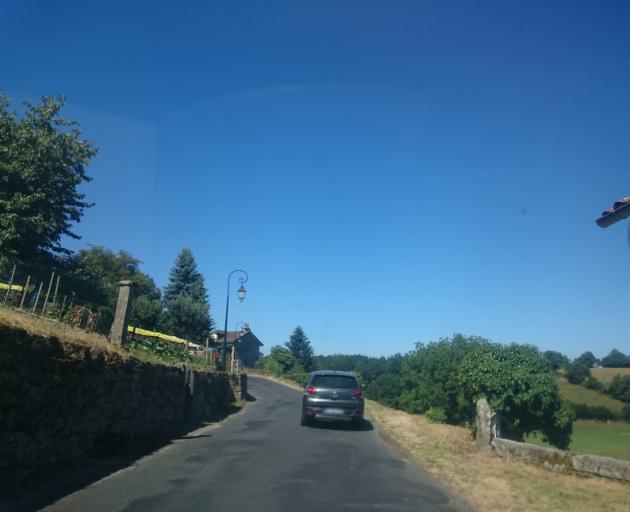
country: FR
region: Auvergne
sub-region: Departement du Cantal
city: Saint-Mamet-la-Salvetat
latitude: 44.7831
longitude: 2.3537
